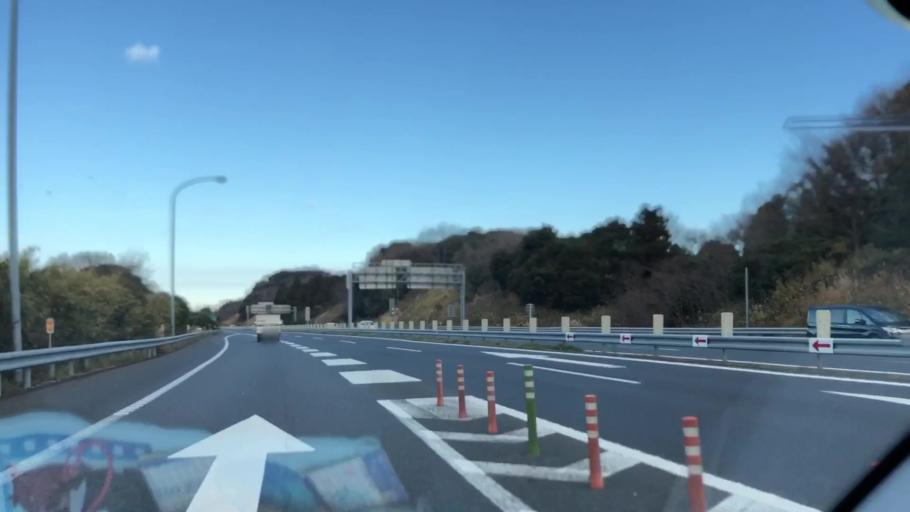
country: JP
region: Chiba
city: Kisarazu
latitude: 35.3809
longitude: 139.9775
